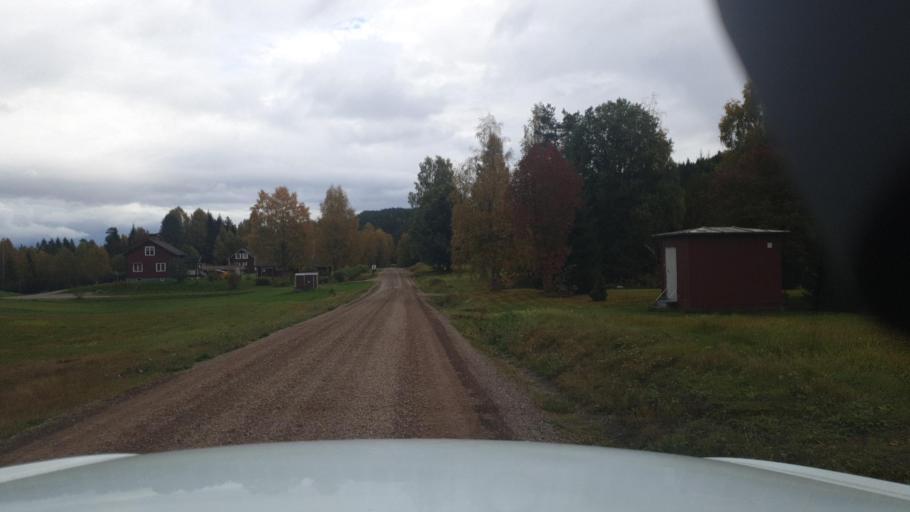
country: SE
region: Vaermland
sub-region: Eda Kommun
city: Charlottenberg
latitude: 60.0739
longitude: 12.5285
